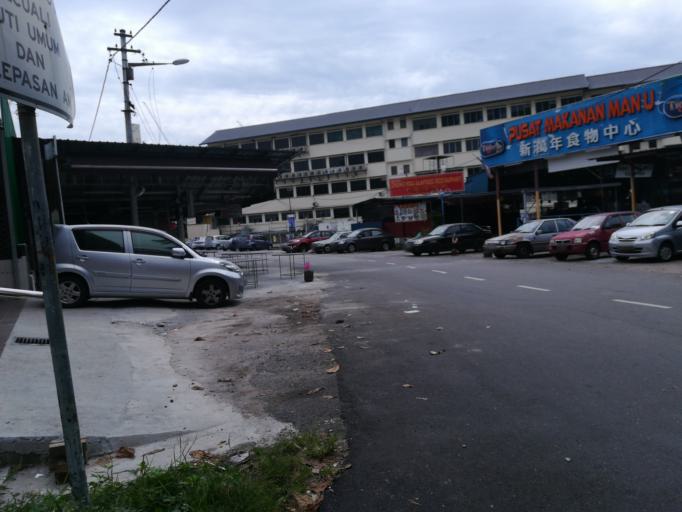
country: MY
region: Perak
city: Ipoh
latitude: 4.5945
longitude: 101.0871
